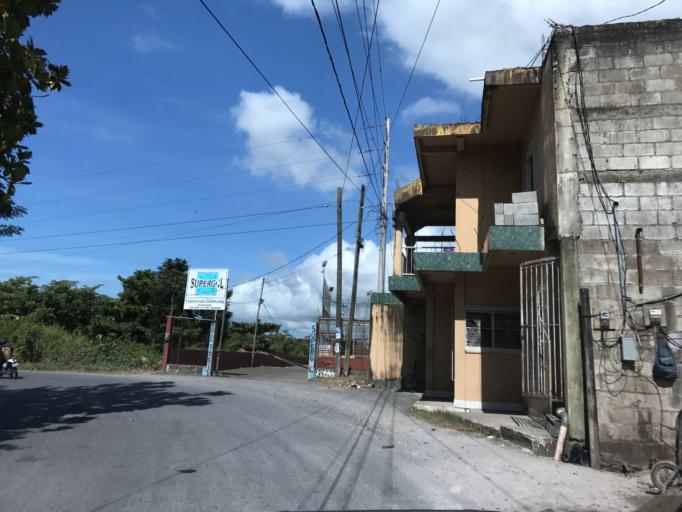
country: GT
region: Izabal
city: Morales
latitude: 15.6570
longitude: -89.0084
